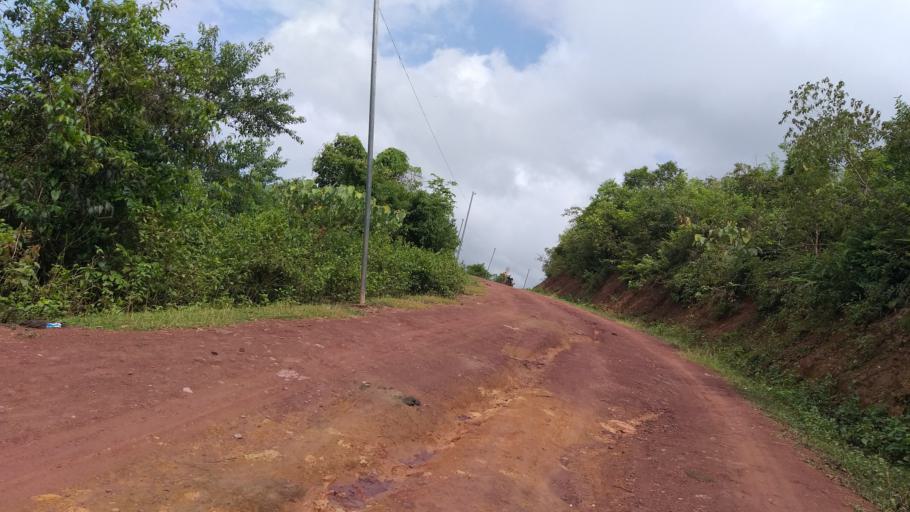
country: LA
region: Phongsali
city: Khoa
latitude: 21.3884
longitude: 102.6382
